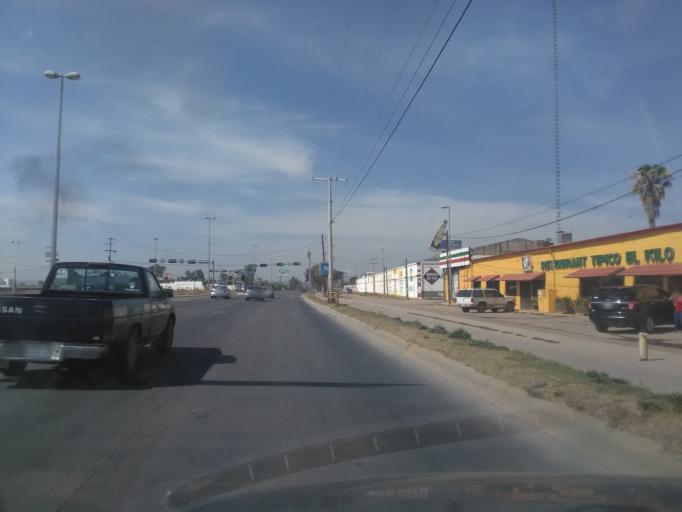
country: MX
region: Durango
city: Victoria de Durango
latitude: 24.0757
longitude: -104.5924
